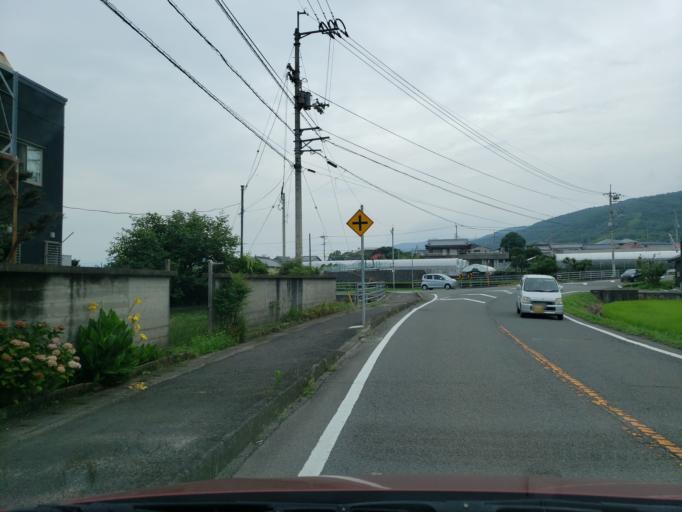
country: JP
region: Tokushima
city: Kamojimacho-jogejima
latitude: 34.1040
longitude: 134.2663
